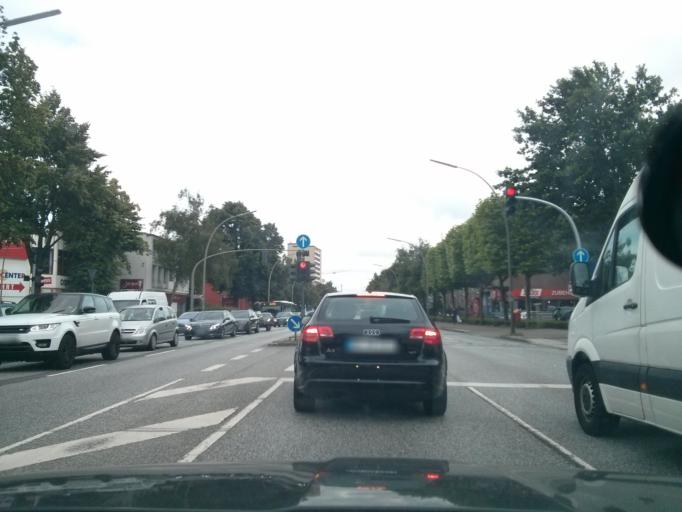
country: DE
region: Hamburg
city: Stellingen
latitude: 53.5877
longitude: 9.9317
